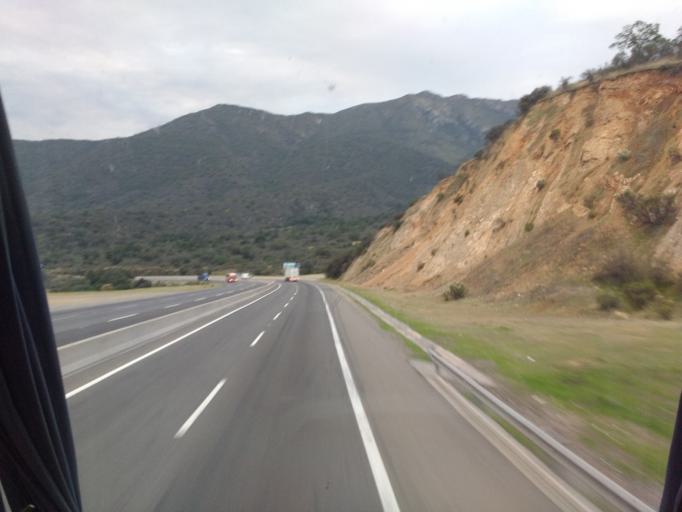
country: CL
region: Santiago Metropolitan
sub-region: Provincia de Talagante
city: Penaflor
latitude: -33.4468
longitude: -70.9817
